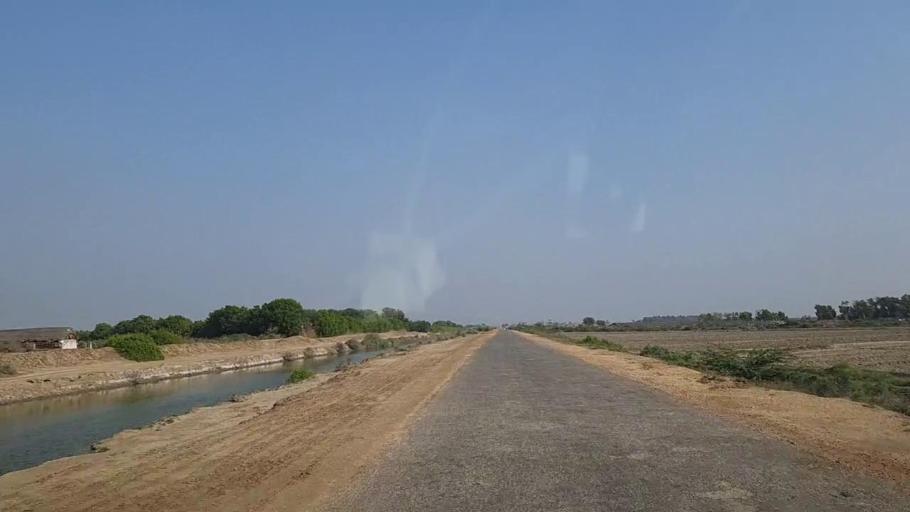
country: PK
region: Sindh
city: Mirpur Sakro
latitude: 24.6365
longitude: 67.6010
